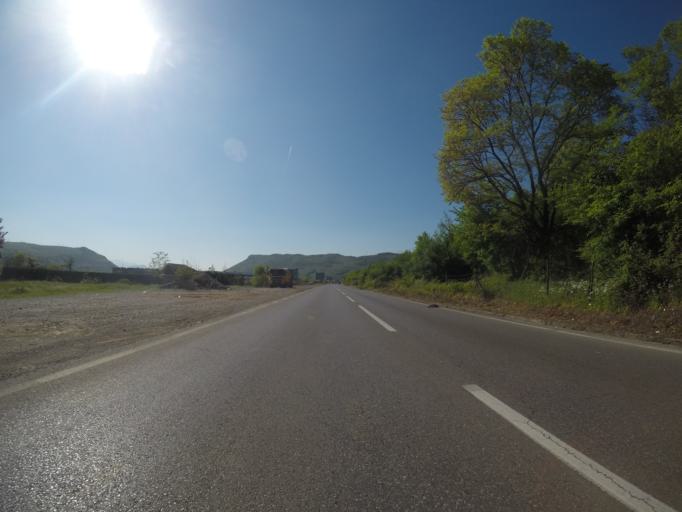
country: ME
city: Spuz
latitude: 42.4732
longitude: 19.1726
